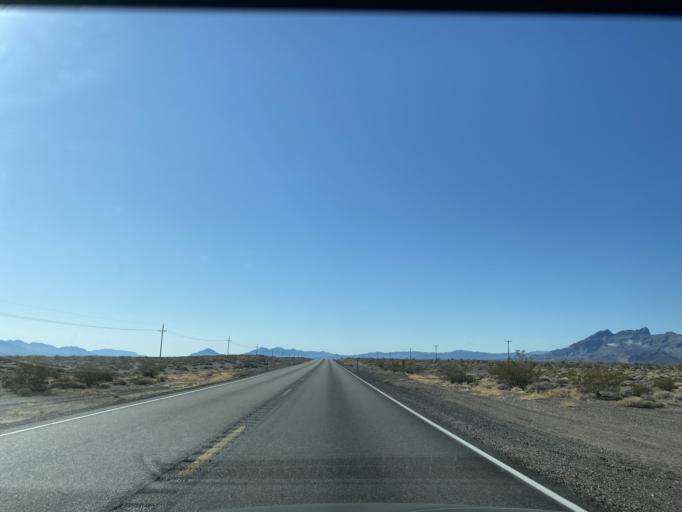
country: US
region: Nevada
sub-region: Nye County
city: Pahrump
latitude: 36.4588
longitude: -116.4218
